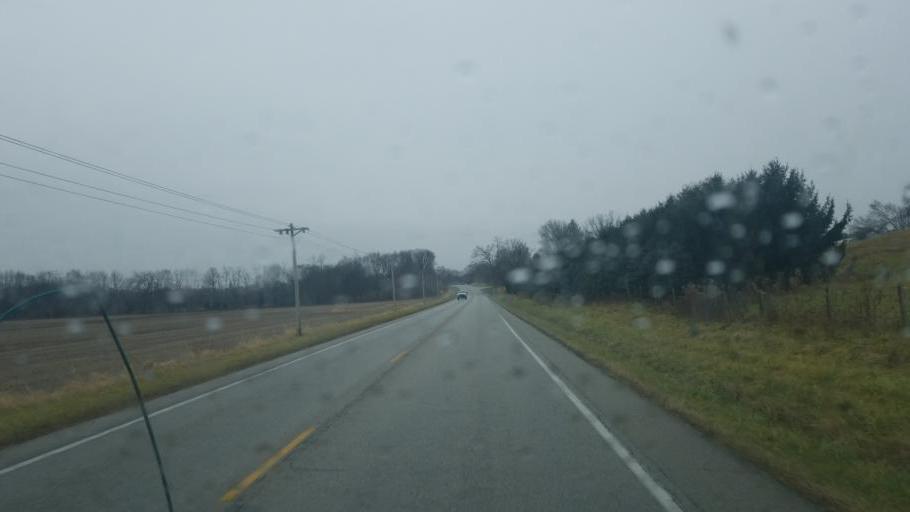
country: US
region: Indiana
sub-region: Shelby County
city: Shelbyville
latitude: 39.5729
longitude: -85.7765
